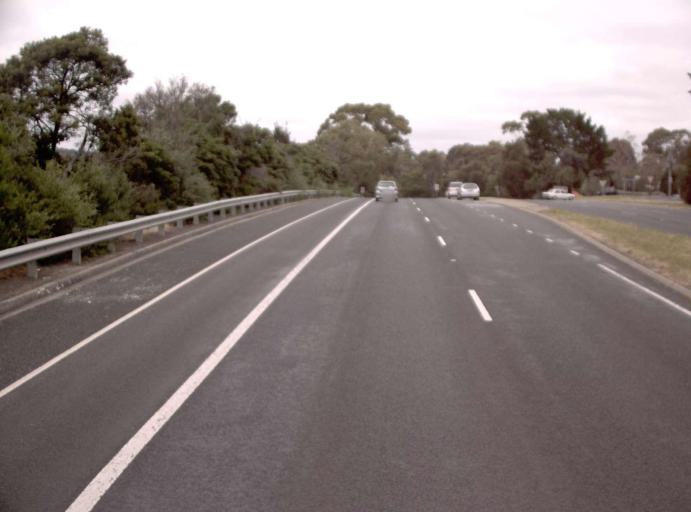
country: AU
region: Victoria
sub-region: Mornington Peninsula
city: Mount Eliza
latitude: -38.1784
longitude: 145.0965
